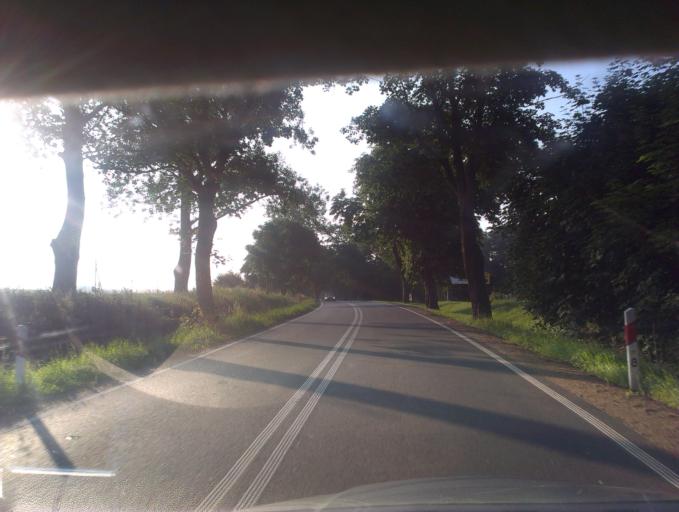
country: PL
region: West Pomeranian Voivodeship
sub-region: Powiat szczecinecki
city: Barwice
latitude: 53.7239
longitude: 16.3932
